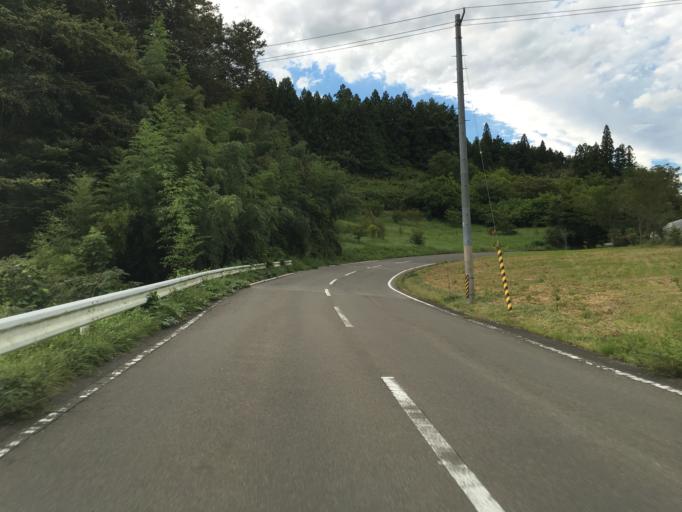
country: JP
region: Fukushima
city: Nihommatsu
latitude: 37.5949
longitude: 140.4963
